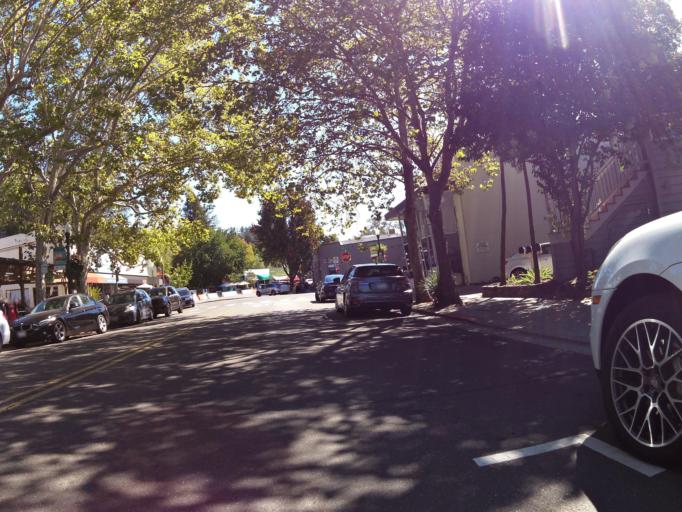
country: US
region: California
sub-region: Marin County
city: San Anselmo
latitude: 37.9763
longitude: -122.5636
